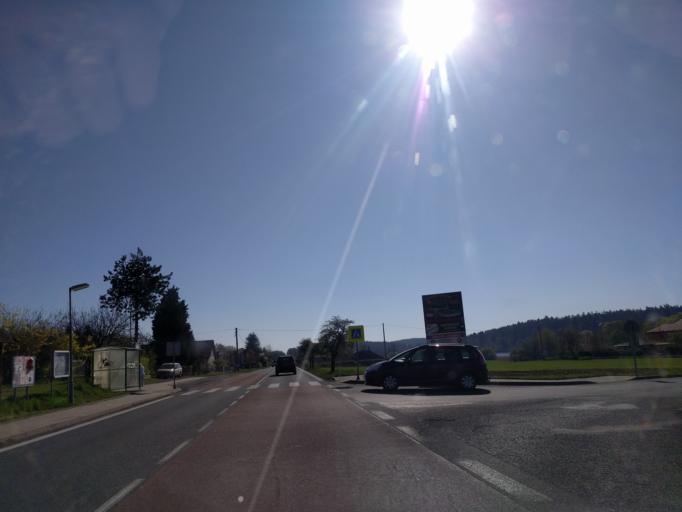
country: CZ
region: Central Bohemia
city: Mukarov
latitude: 49.9890
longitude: 14.7565
